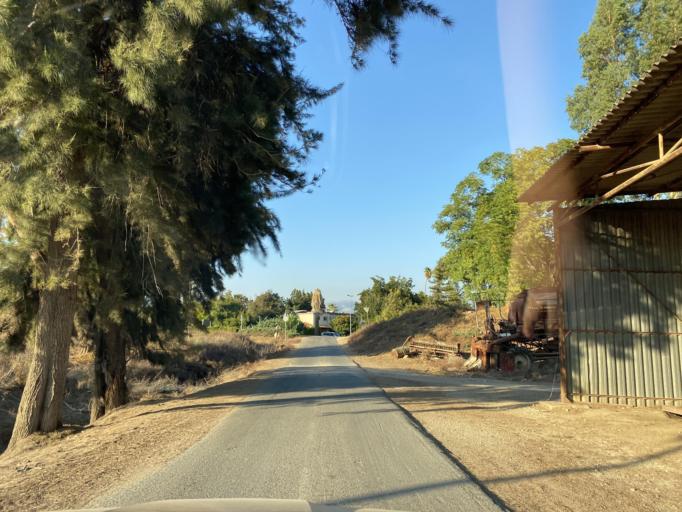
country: IL
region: Northern District
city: Qiryat Shemona
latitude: 33.1725
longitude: 35.6064
